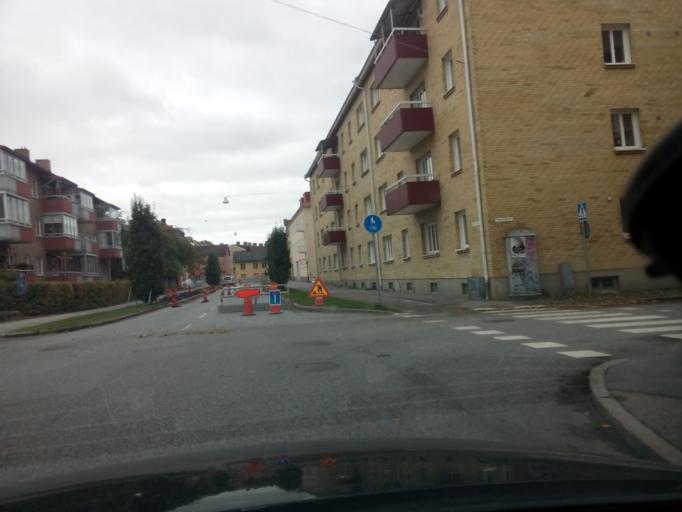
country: SE
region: Soedermanland
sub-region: Nykopings Kommun
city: Nykoping
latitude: 58.7565
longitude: 17.0173
